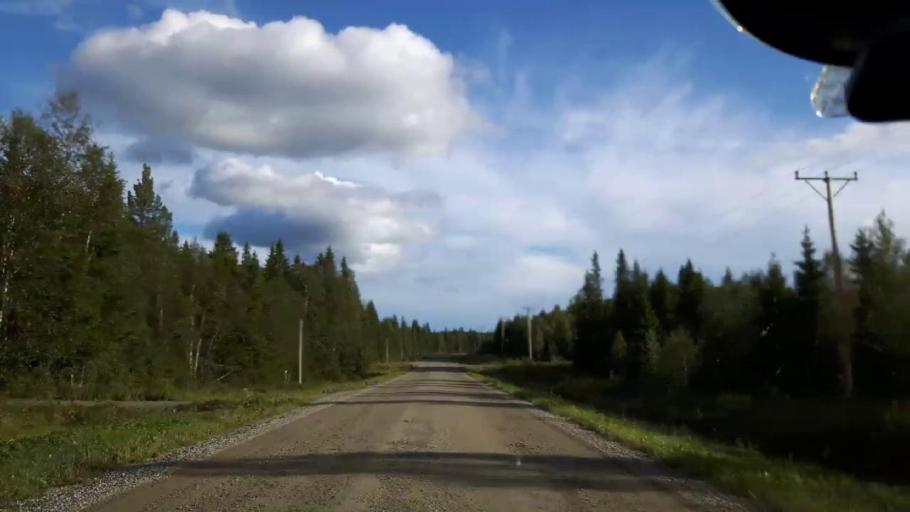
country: SE
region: Jaemtland
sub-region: Stroemsunds Kommun
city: Stroemsund
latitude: 63.3055
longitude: 15.5489
